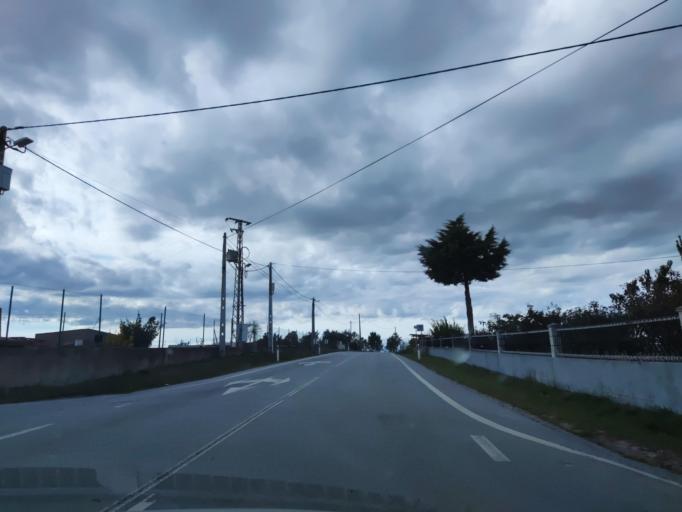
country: ES
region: Castille and Leon
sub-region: Provincia de Salamanca
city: Aldea del Obispo
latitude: 40.6751
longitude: -6.8651
